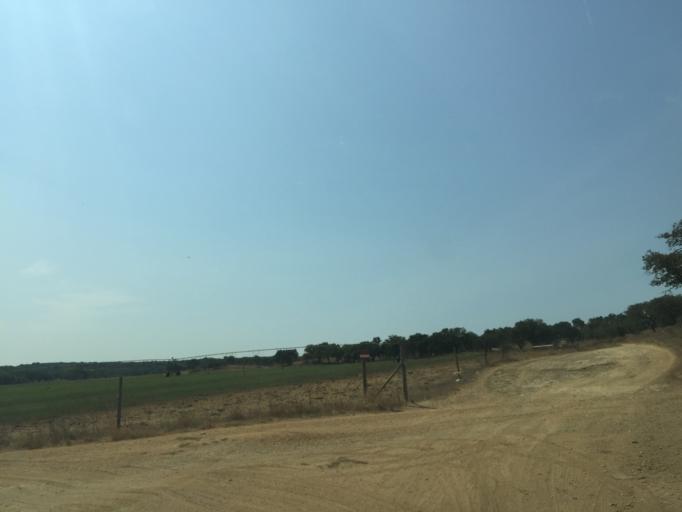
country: PT
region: Setubal
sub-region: Santiago do Cacem
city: Santiago do Cacem
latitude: 37.9730
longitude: -8.5035
